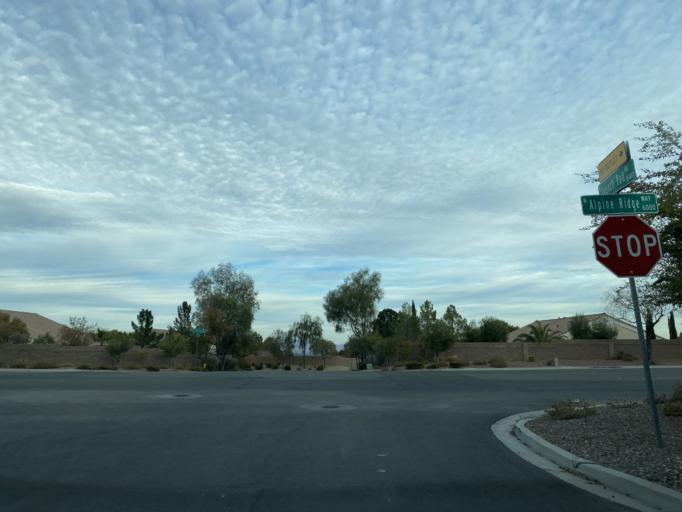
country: US
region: Nevada
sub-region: Clark County
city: Summerlin South
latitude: 36.2754
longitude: -115.3245
